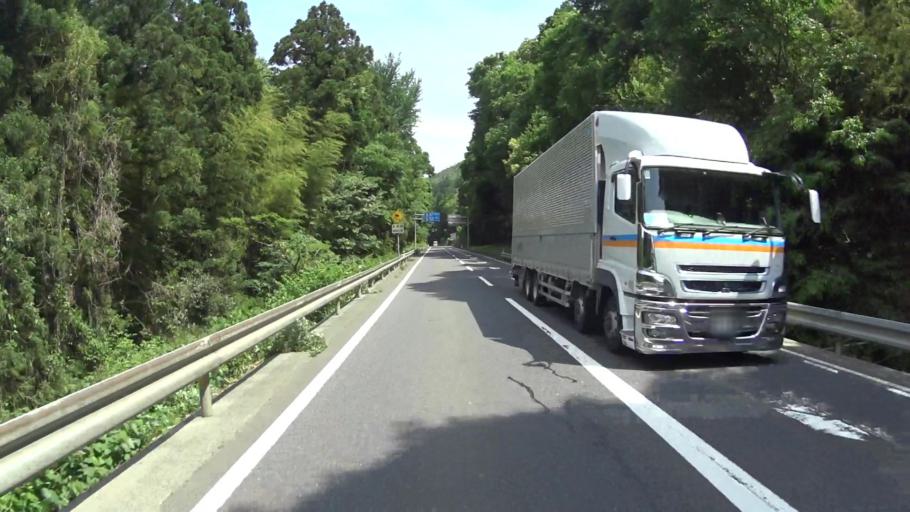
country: JP
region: Fukui
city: Obama
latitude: 35.4714
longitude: 135.8065
